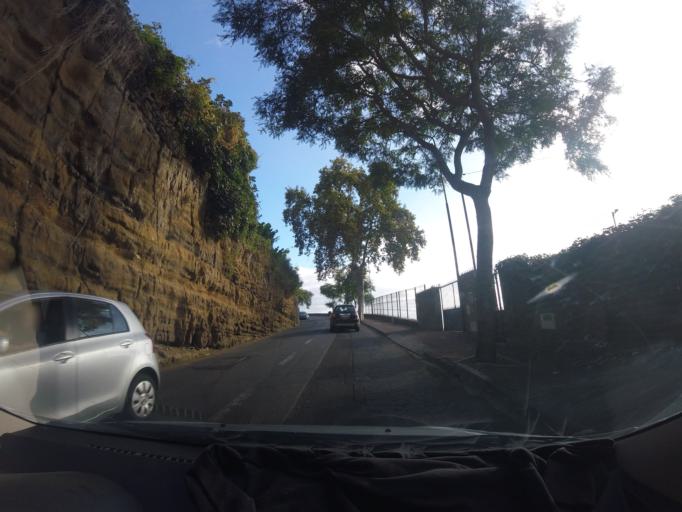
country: PT
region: Madeira
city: Camara de Lobos
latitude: 32.6451
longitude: -16.9608
